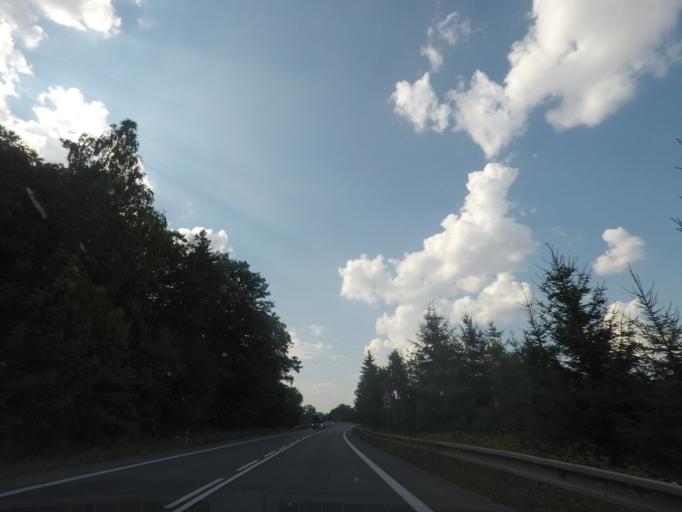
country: CZ
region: Kralovehradecky
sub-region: Okres Nachod
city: Jaromer
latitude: 50.3869
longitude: 15.9090
